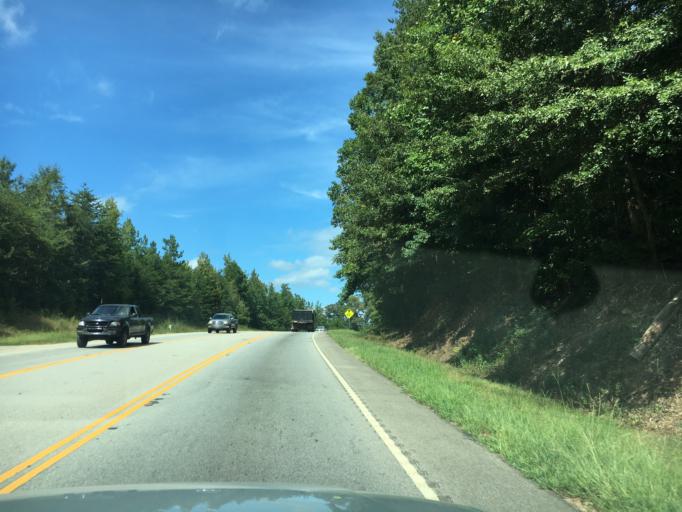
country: US
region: South Carolina
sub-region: Spartanburg County
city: Wellford
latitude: 34.9784
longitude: -82.1170
